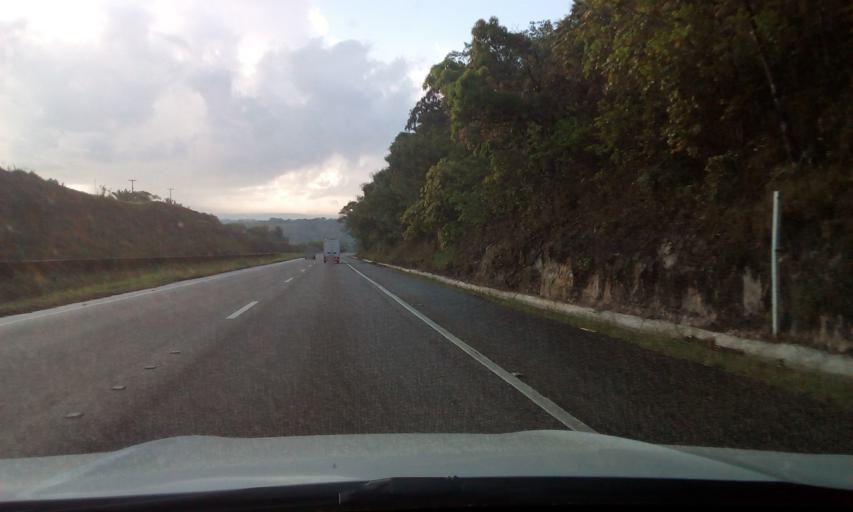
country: BR
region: Pernambuco
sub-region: Itapissuma
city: Itapissuma
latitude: -7.6834
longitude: -34.9244
